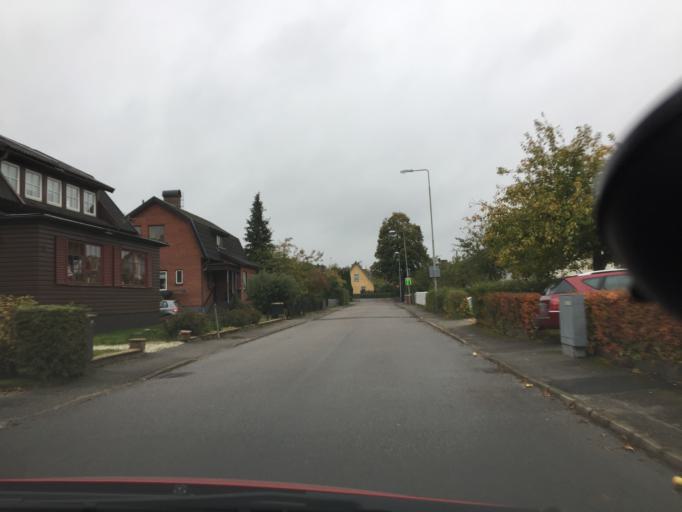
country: SE
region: Vaestra Goetaland
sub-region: Trollhattan
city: Trollhattan
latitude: 58.2912
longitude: 12.3077
